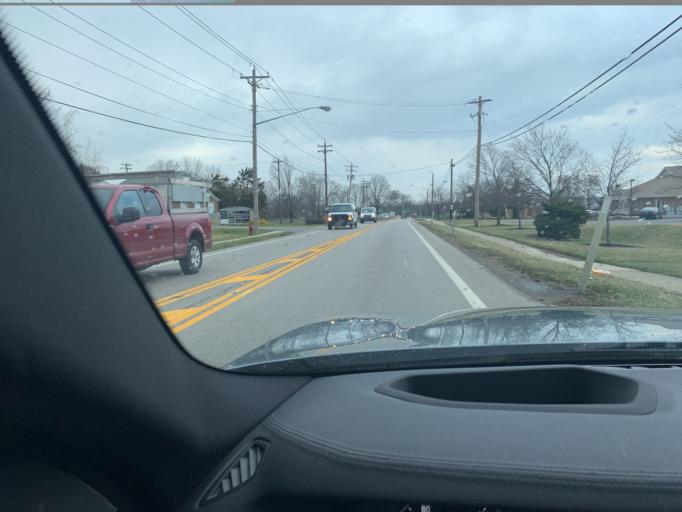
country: US
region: Ohio
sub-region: Hamilton County
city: Springdale
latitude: 39.2793
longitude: -84.4832
